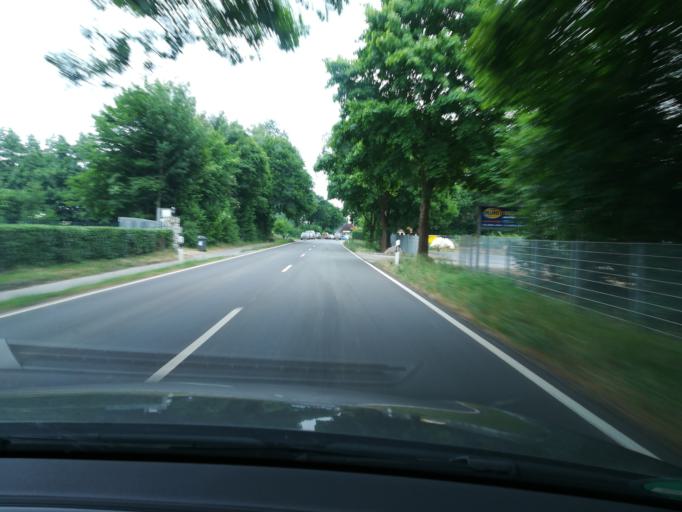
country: DE
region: Schleswig-Holstein
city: Grossensee
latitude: 53.6214
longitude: 10.3346
